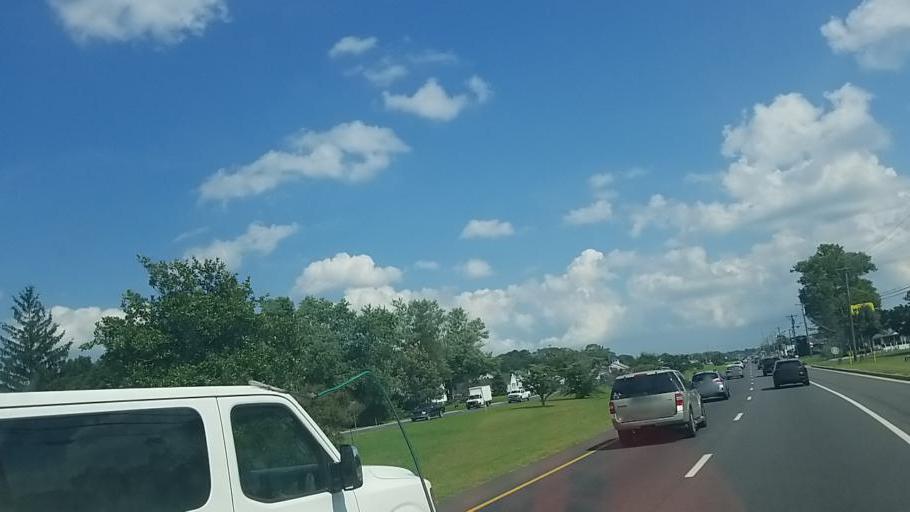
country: US
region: Delaware
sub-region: Sussex County
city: Millsboro
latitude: 38.5928
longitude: -75.3085
